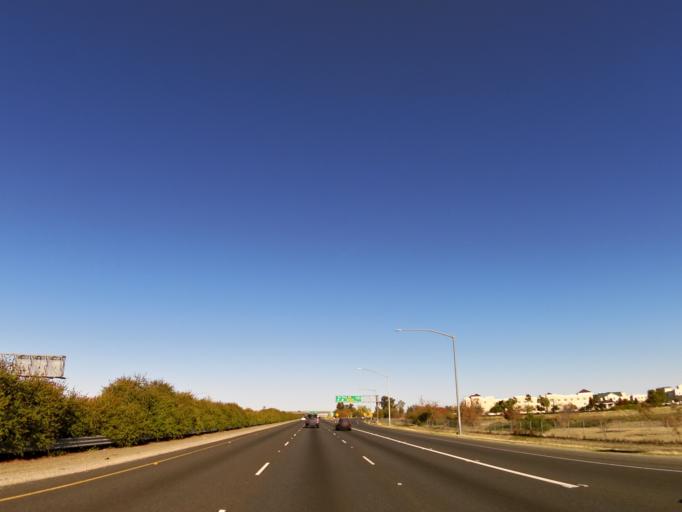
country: US
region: California
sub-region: Yolo County
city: West Sacramento
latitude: 38.6505
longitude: -121.5305
